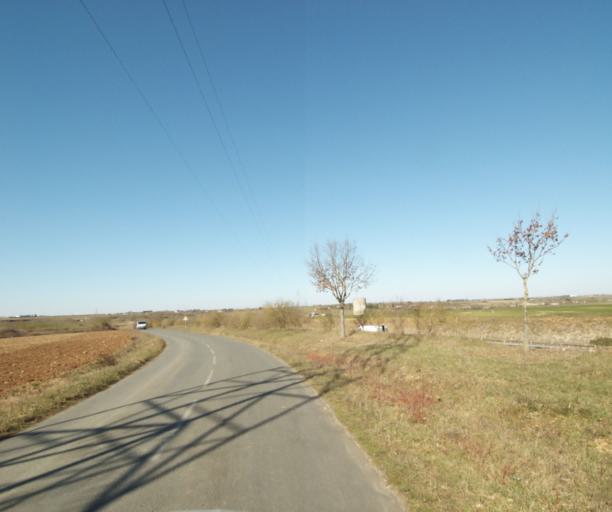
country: FR
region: Poitou-Charentes
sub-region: Departement des Deux-Sevres
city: Bessines
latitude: 46.3357
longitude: -0.5037
